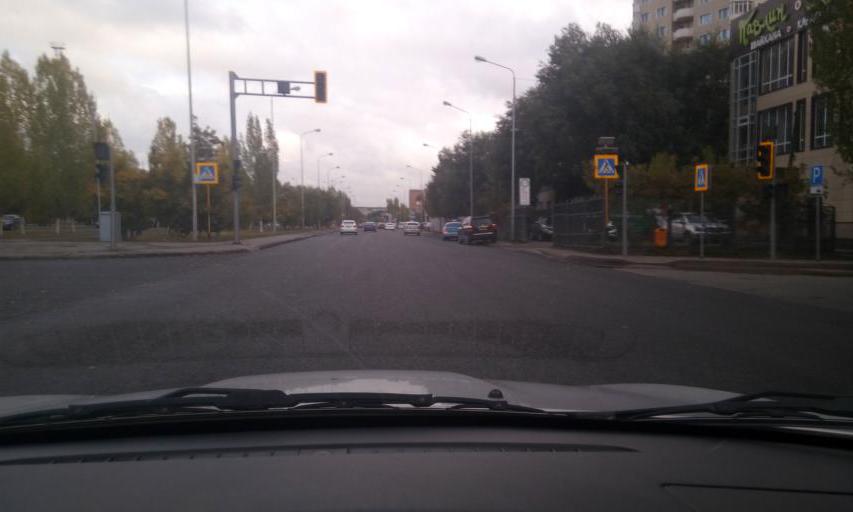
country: KZ
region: Astana Qalasy
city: Astana
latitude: 51.1653
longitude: 71.4660
